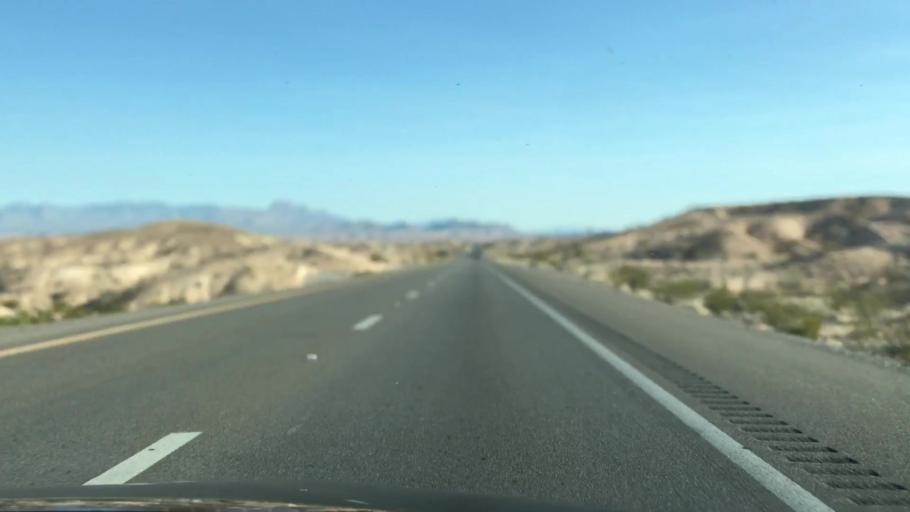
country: US
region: Nevada
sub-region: Clark County
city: Moapa Town
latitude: 36.6034
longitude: -114.6364
